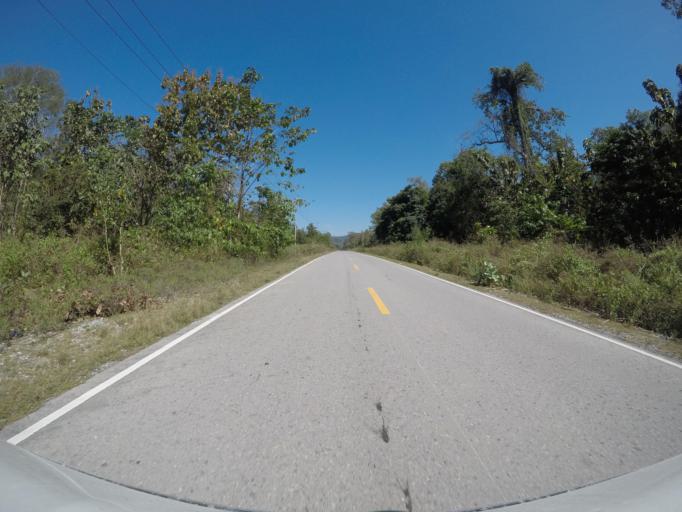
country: TL
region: Viqueque
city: Viqueque
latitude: -8.9655
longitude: 126.0214
